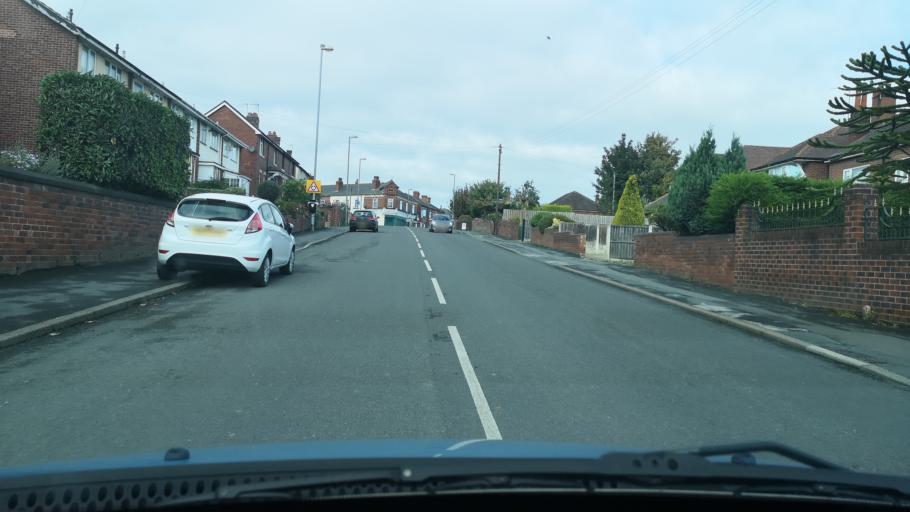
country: GB
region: England
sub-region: City and Borough of Wakefield
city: Normanton
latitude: 53.7041
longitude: -1.4283
